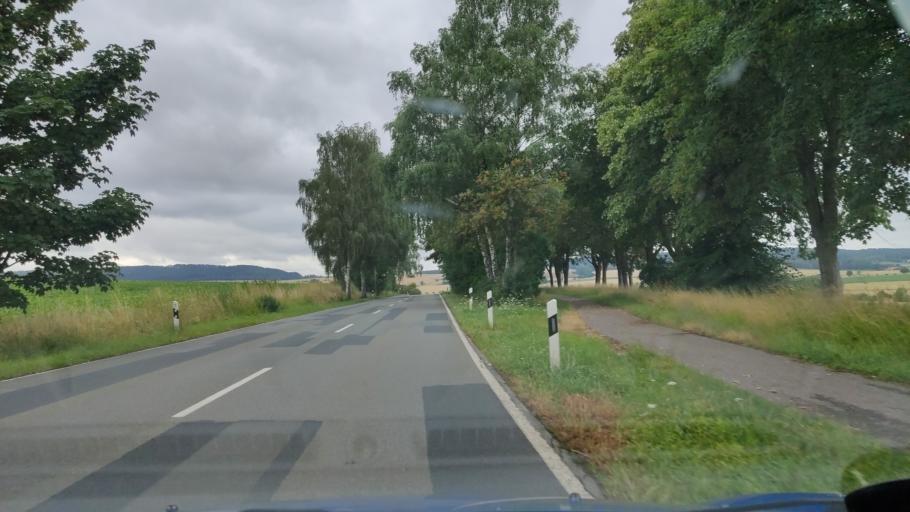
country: DE
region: Lower Saxony
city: Coppenbrugge
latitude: 52.0979
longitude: 9.4968
